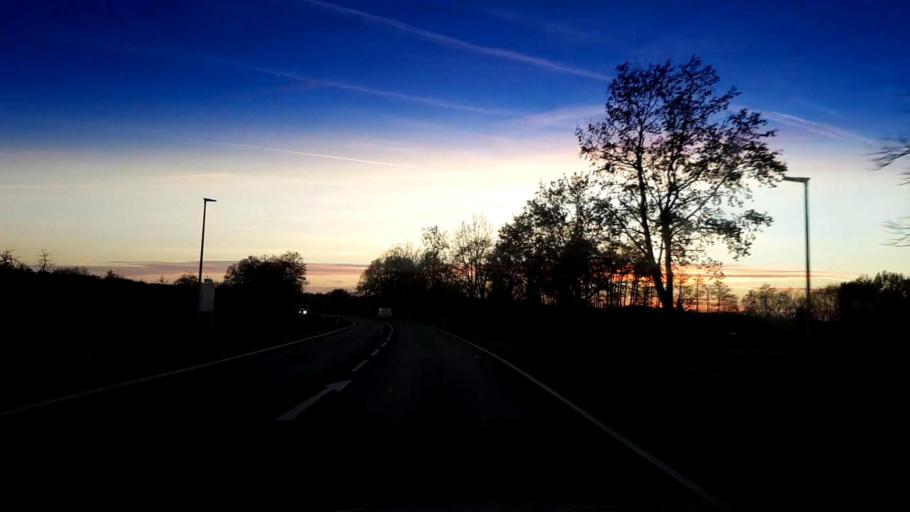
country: DE
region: Bavaria
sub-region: Upper Franconia
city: Memmelsdorf
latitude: 49.9285
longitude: 10.9436
